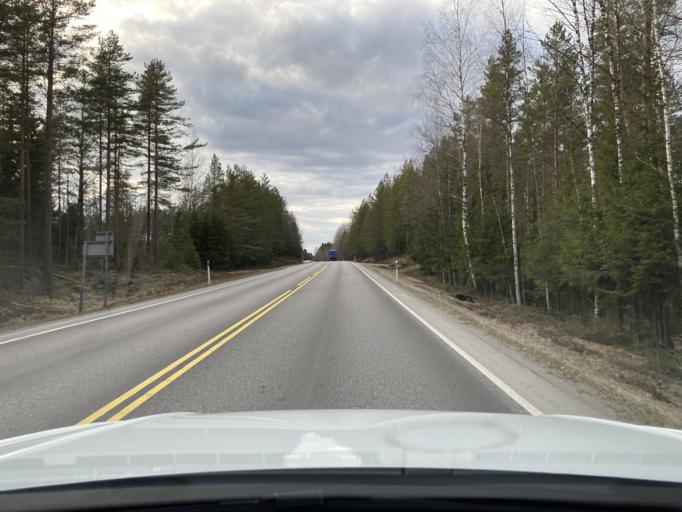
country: FI
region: Haeme
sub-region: Haemeenlinna
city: Renko
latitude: 60.8006
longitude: 24.0823
